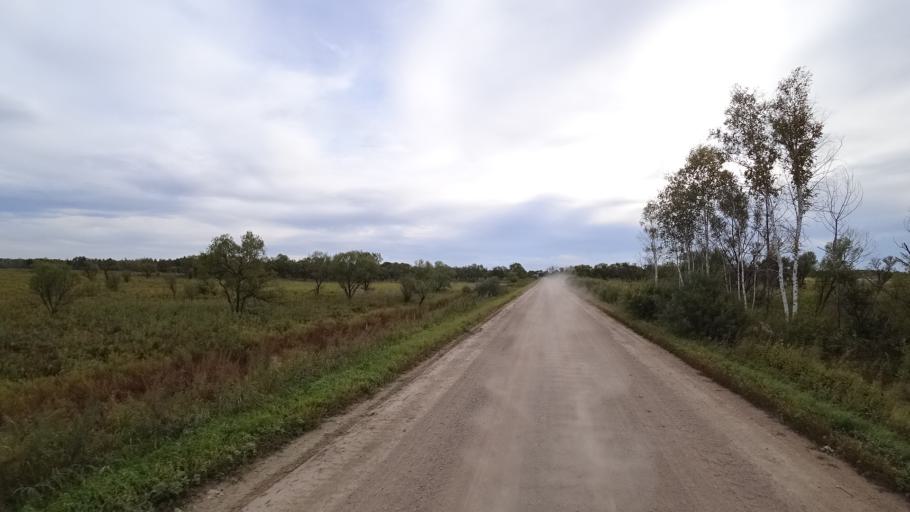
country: RU
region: Amur
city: Arkhara
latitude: 49.3767
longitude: 130.2102
